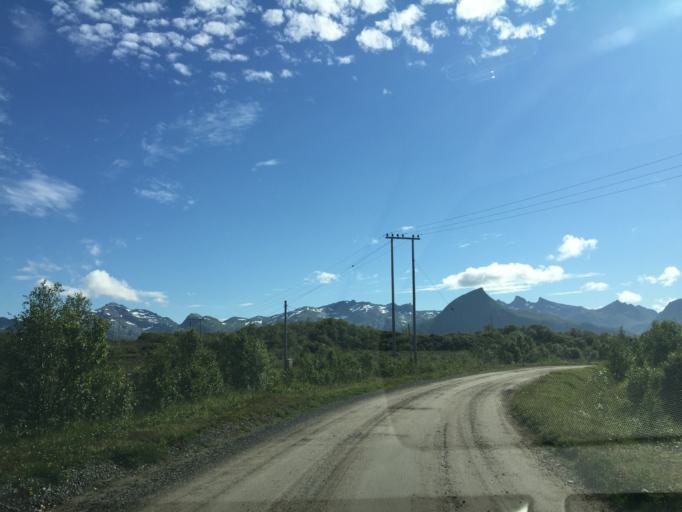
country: NO
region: Nordland
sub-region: Vagan
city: Kabelvag
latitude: 68.3572
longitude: 14.4505
